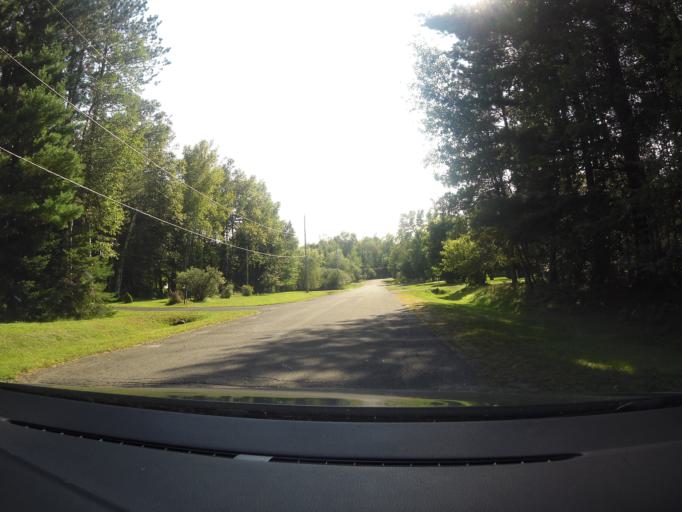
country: CA
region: Ontario
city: Carleton Place
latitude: 45.2967
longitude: -76.0612
